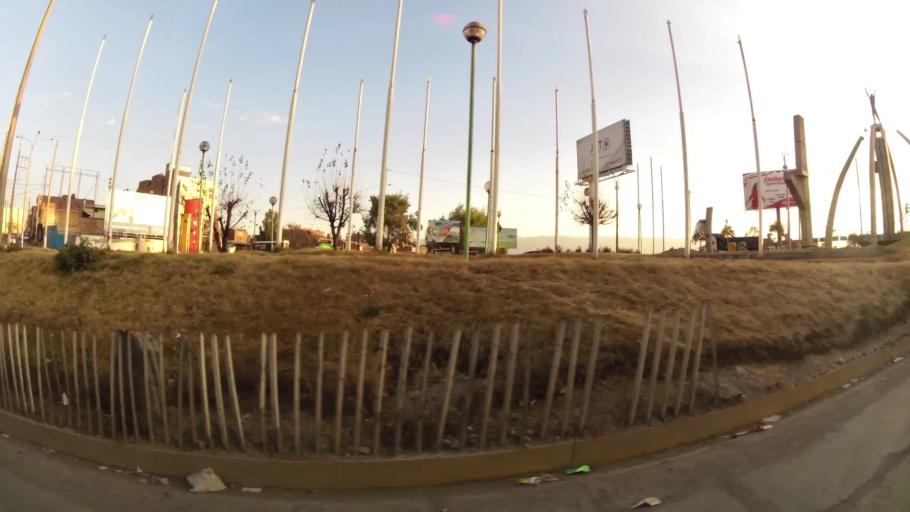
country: PE
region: Junin
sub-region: Provincia de Huancayo
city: El Tambo
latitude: -12.0531
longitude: -75.2257
